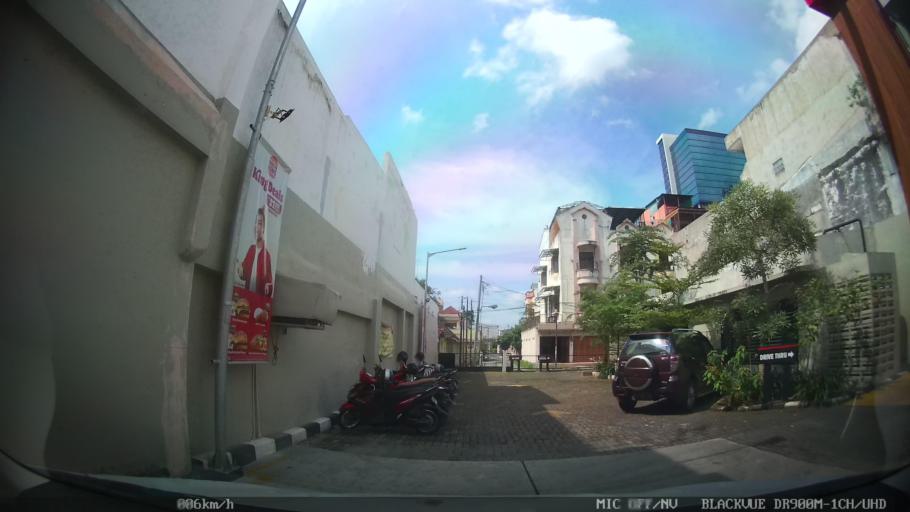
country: ID
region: North Sumatra
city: Medan
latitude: 3.5847
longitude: 98.6654
